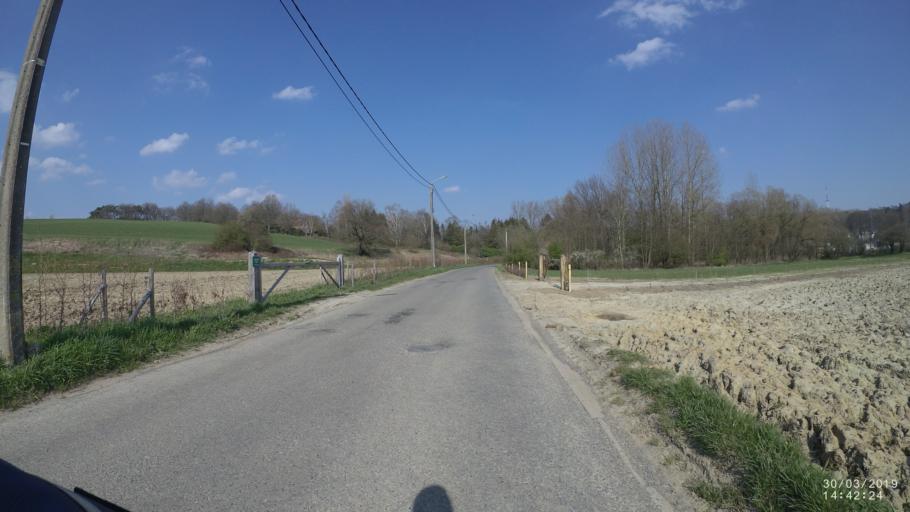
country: BE
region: Wallonia
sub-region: Province du Brabant Wallon
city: Rixensart
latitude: 50.7391
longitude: 4.5547
